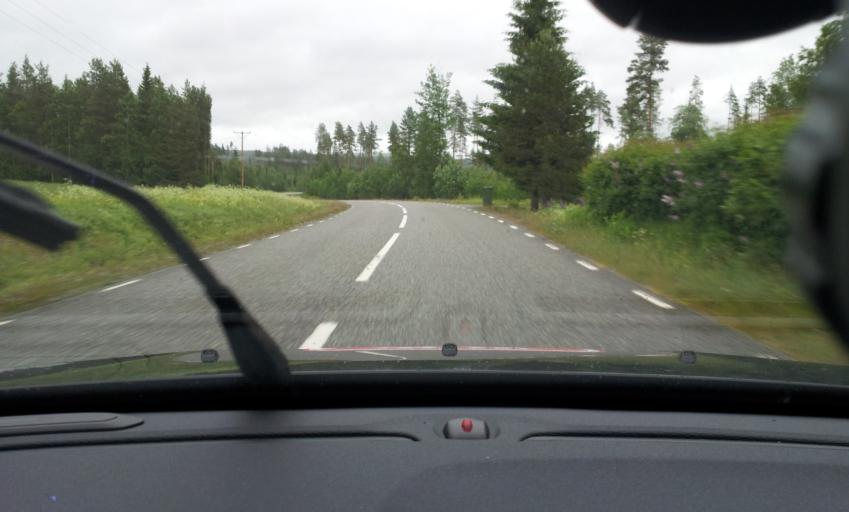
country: SE
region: Jaemtland
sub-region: Ragunda Kommun
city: Hammarstrand
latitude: 63.2646
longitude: 15.8599
